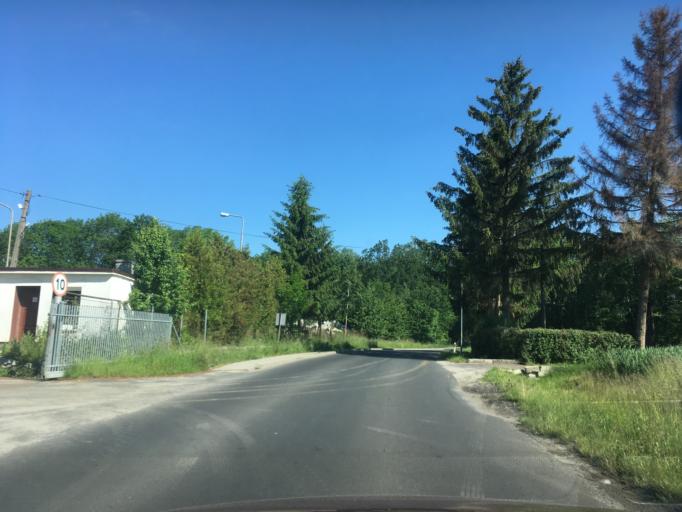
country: PL
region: Lower Silesian Voivodeship
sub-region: Powiat zgorzelecki
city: Zgorzelec
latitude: 51.1145
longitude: 15.0275
